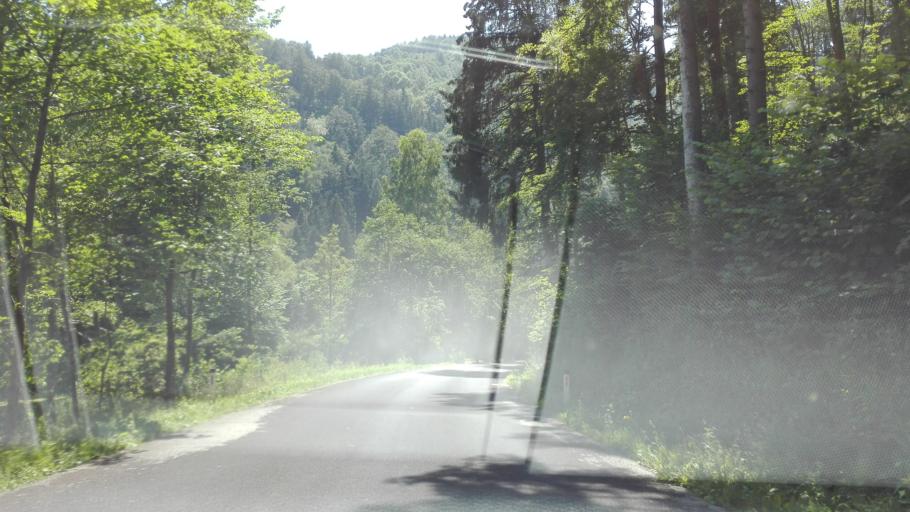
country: AT
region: Upper Austria
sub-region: Politischer Bezirk Rohrbach
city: Kleinzell im Muehlkreis
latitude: 48.3757
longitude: 13.9488
